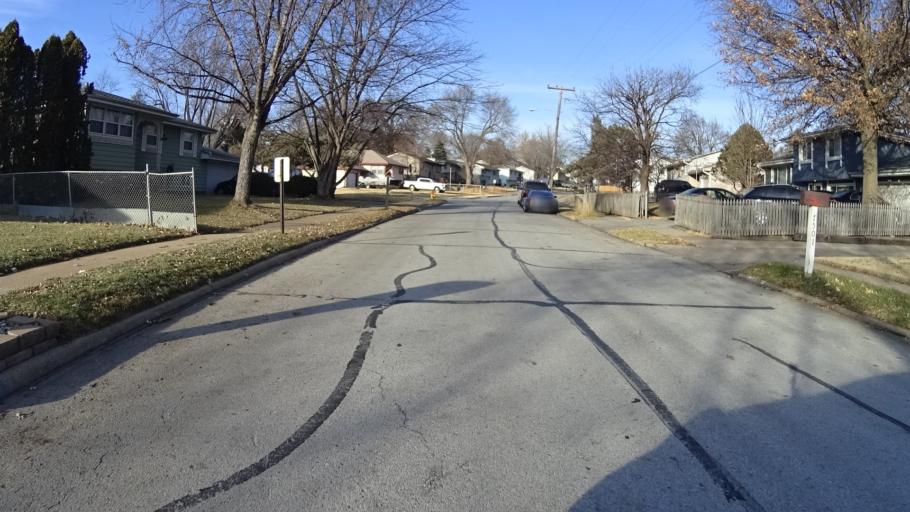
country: US
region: Nebraska
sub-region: Sarpy County
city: La Vista
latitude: 41.1851
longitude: -95.9956
